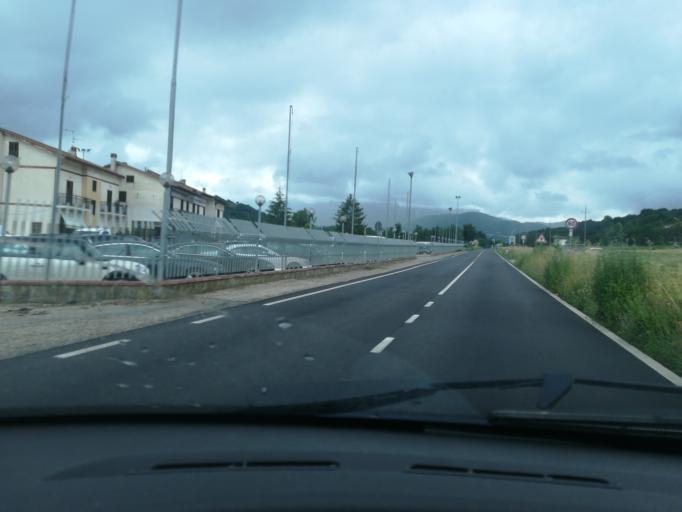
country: IT
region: The Marches
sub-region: Provincia di Macerata
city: San Ginesio
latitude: 43.0904
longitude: 13.3137
